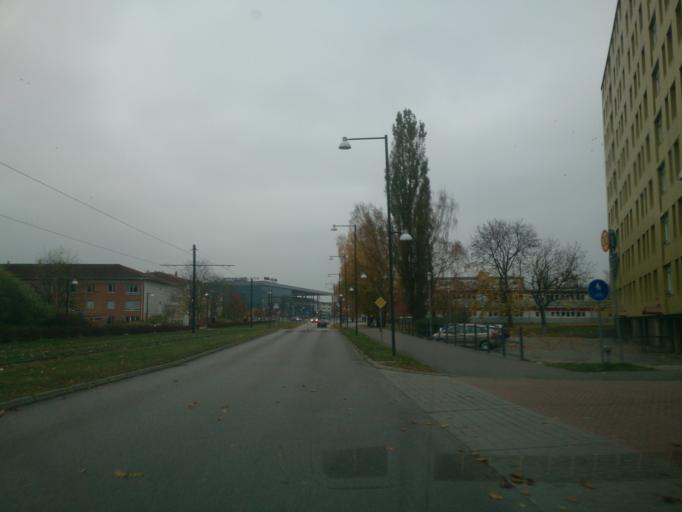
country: SE
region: OEstergoetland
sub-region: Norrkopings Kommun
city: Norrkoping
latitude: 58.5742
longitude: 16.2032
